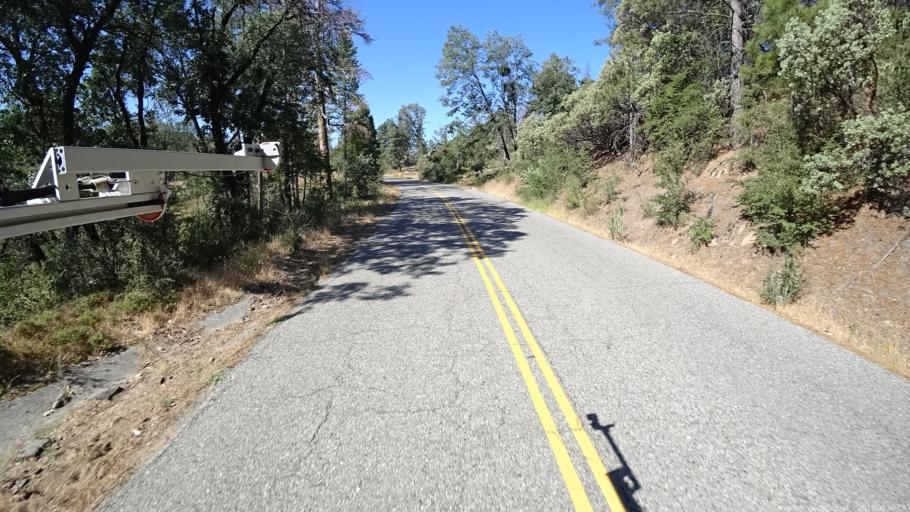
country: US
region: California
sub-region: Fresno County
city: Auberry
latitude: 37.2090
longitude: -119.4024
